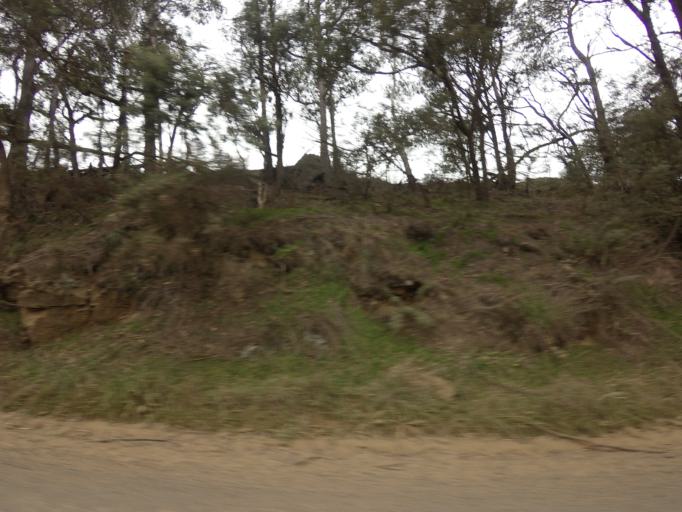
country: AU
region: Tasmania
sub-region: Derwent Valley
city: New Norfolk
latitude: -42.5809
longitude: 147.0068
